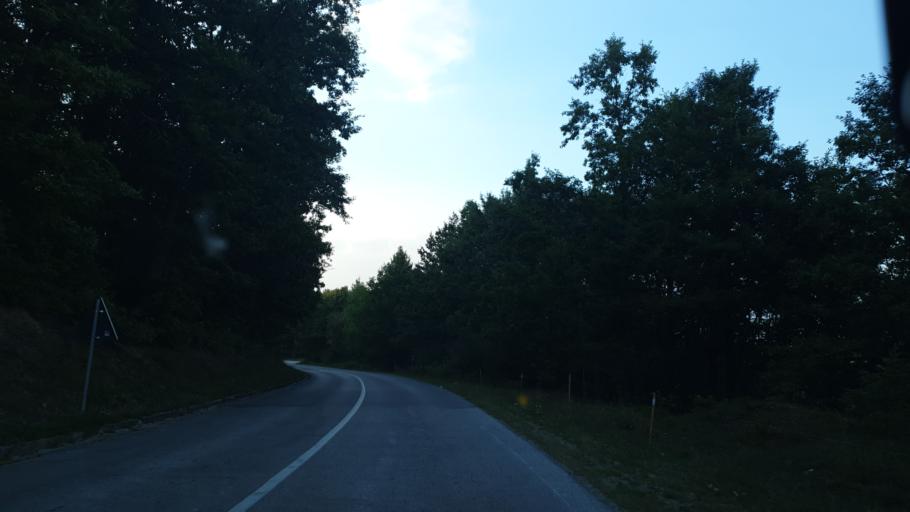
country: RS
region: Central Serbia
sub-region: Zlatiborski Okrug
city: Kosjeric
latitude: 44.0265
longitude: 20.0122
